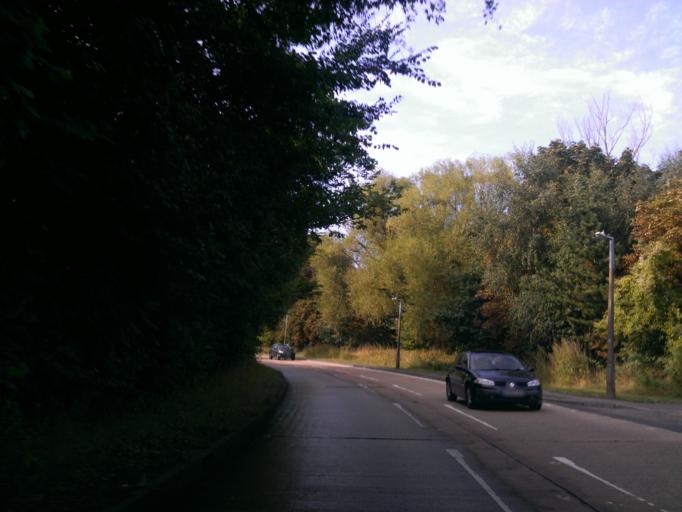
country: GB
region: England
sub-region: Essex
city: Witham
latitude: 51.8181
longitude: 0.6677
